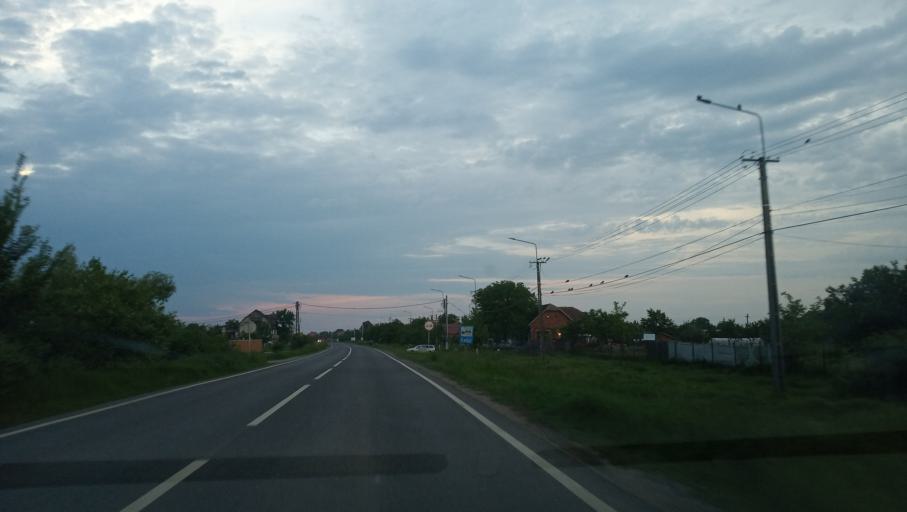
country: RO
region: Timis
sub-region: Comuna Jebel
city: Jebel
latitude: 45.5518
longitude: 21.2223
